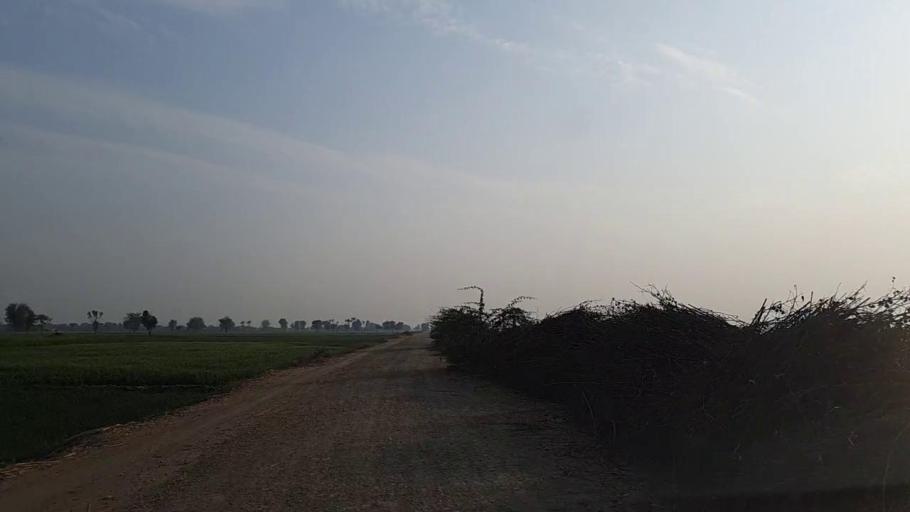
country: PK
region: Sindh
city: Jam Sahib
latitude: 26.3187
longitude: 68.5337
